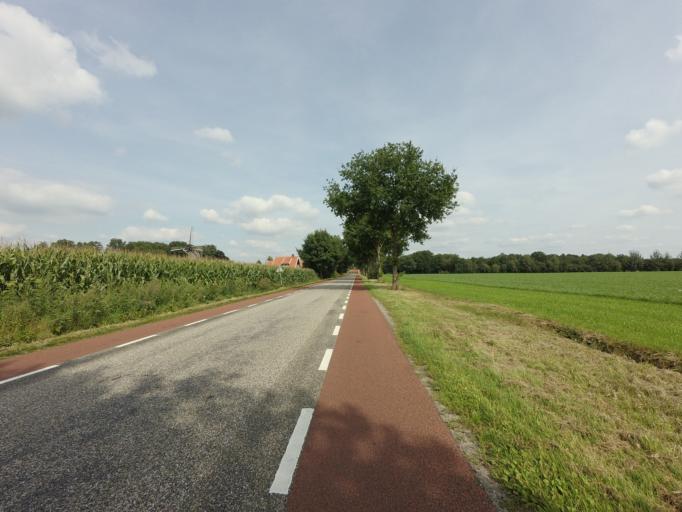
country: DE
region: Lower Saxony
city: Lage
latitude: 52.4134
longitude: 6.9588
